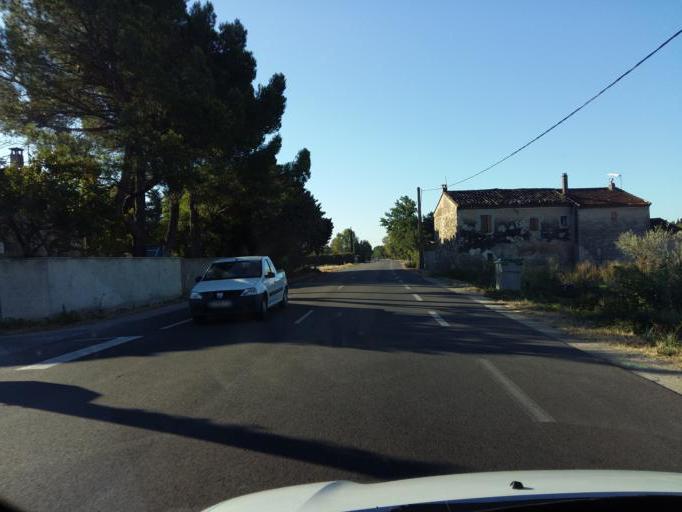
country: FR
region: Provence-Alpes-Cote d'Azur
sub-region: Departement du Vaucluse
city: Monteux
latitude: 44.0182
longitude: 5.0063
